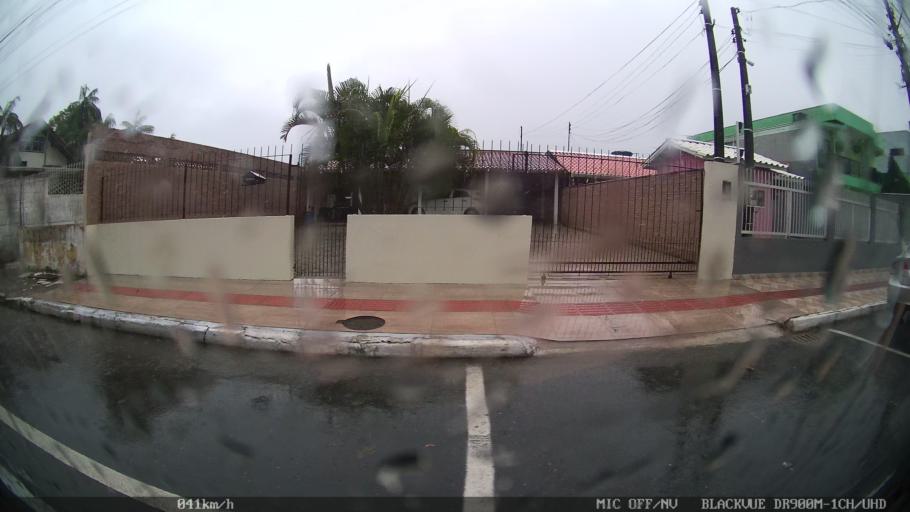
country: BR
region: Santa Catarina
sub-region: Balneario Camboriu
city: Balneario Camboriu
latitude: -27.0116
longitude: -48.6328
